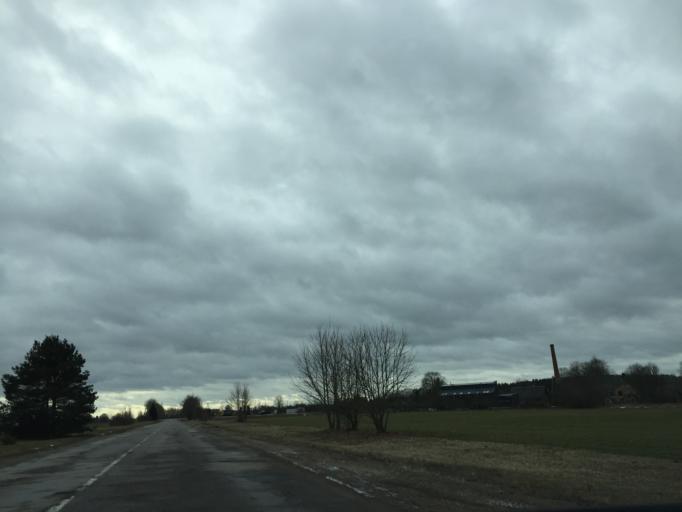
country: LV
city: Tervete
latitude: 56.4800
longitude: 23.3956
